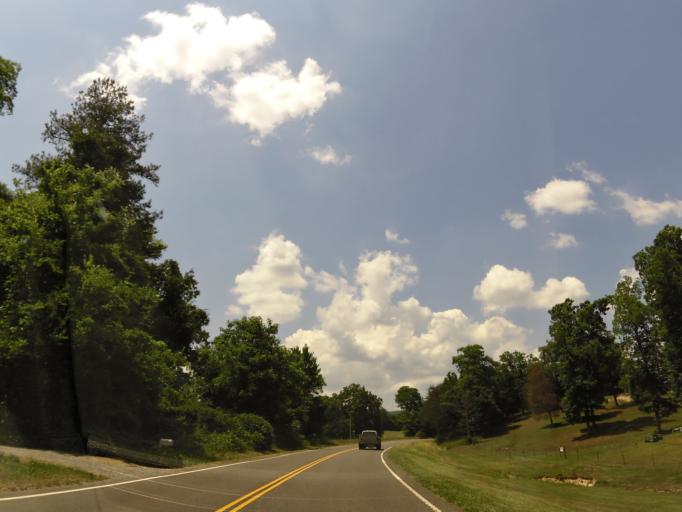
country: US
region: Tennessee
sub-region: Rhea County
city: Spring City
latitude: 35.6518
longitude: -84.8797
